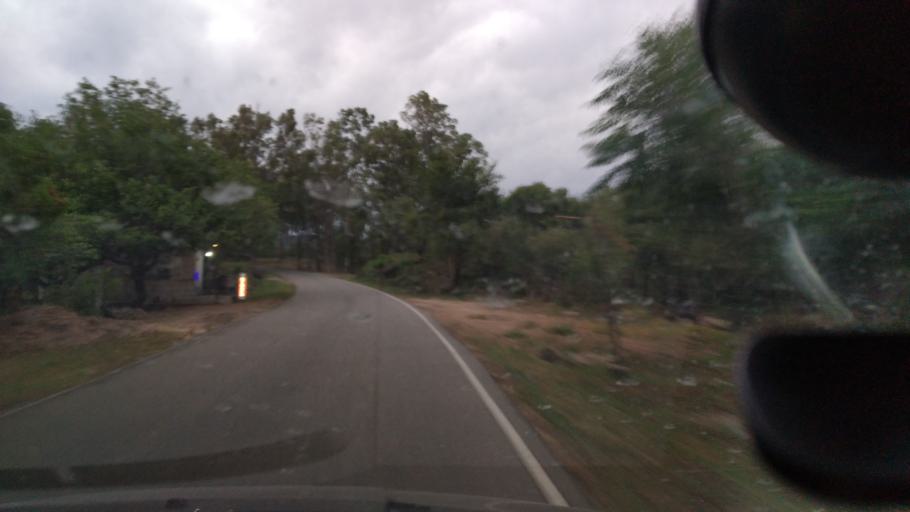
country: AR
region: Cordoba
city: Villa Las Rosas
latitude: -31.8814
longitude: -65.0237
